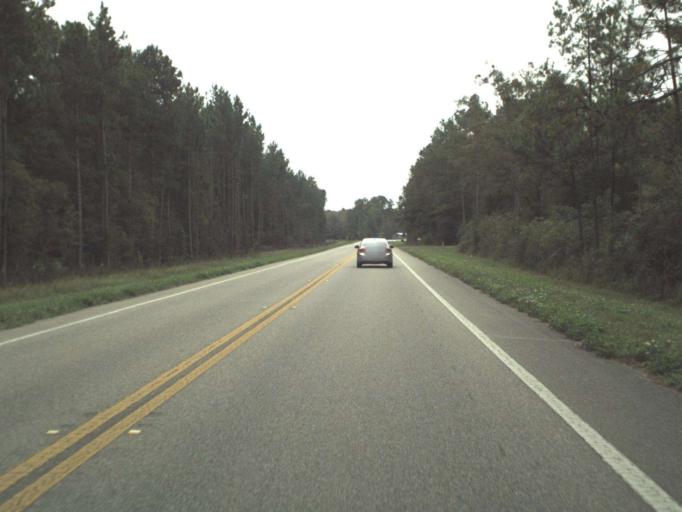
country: US
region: Florida
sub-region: Calhoun County
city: Blountstown
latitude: 30.5226
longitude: -85.0310
